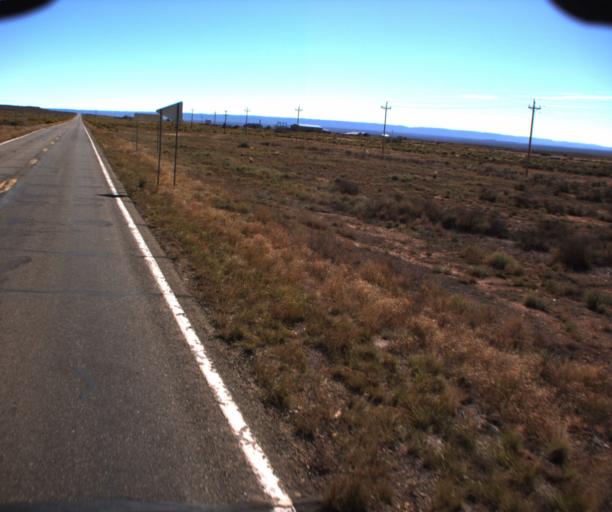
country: US
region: Arizona
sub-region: Coconino County
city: Fredonia
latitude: 36.9381
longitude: -112.5166
